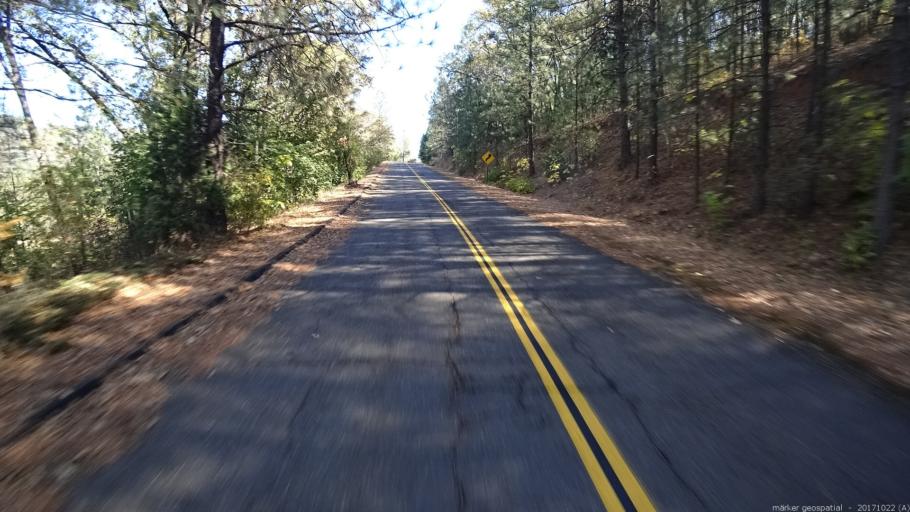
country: US
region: California
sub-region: Shasta County
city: Central Valley (historical)
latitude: 40.9207
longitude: -122.4052
